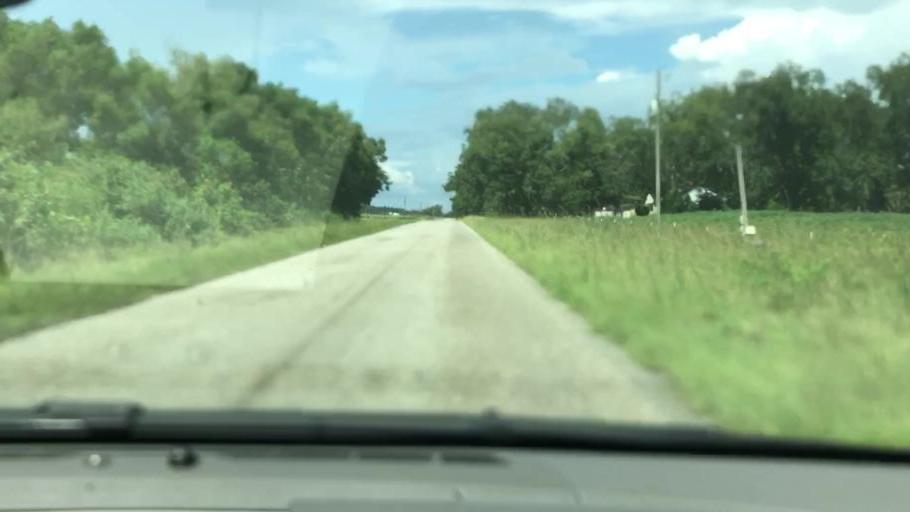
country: US
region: Georgia
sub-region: Early County
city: Blakely
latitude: 31.2063
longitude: -85.0035
